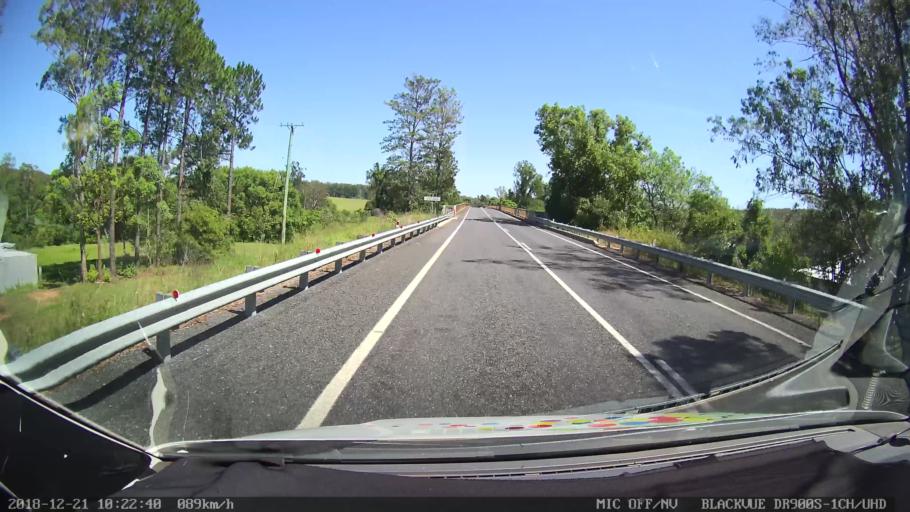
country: AU
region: New South Wales
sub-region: Clarence Valley
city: South Grafton
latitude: -29.6513
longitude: 152.7995
